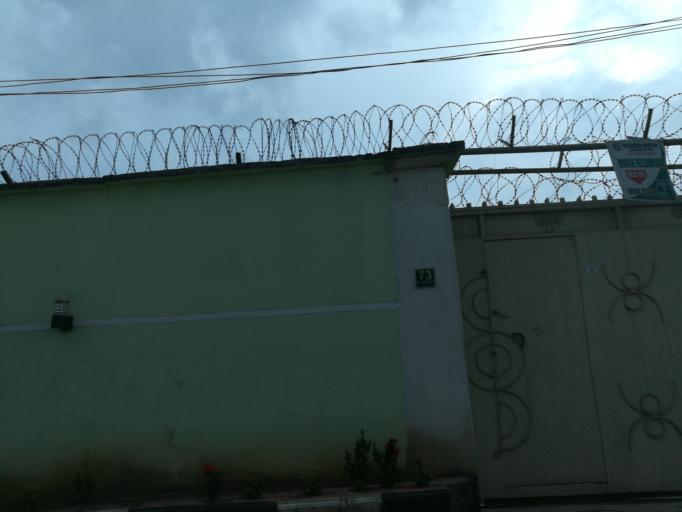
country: NG
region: Rivers
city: Port Harcourt
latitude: 4.8169
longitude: 7.0698
